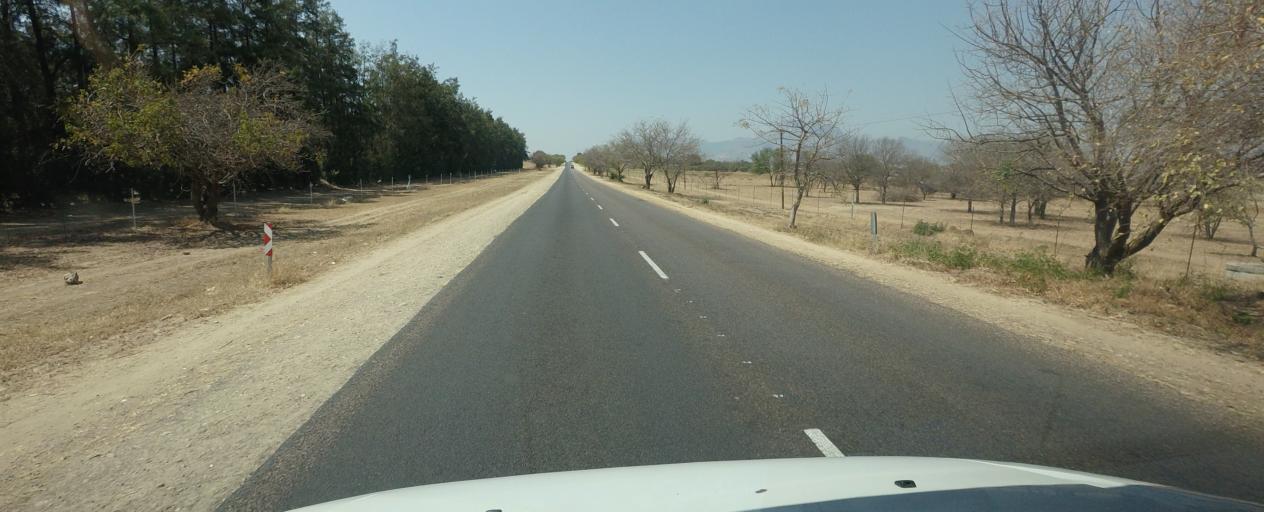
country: ZA
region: Limpopo
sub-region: Mopani District Municipality
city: Hoedspruit
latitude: -24.4237
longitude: 30.8398
